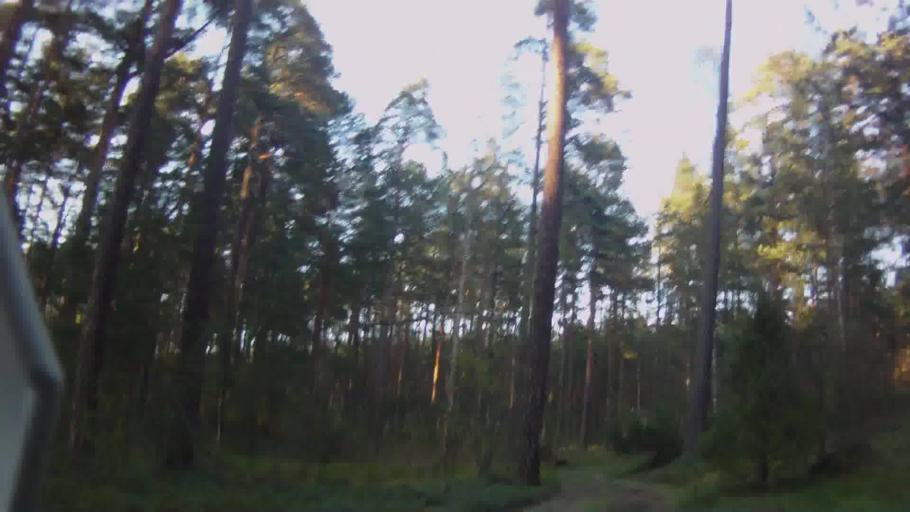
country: LV
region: Riga
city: Jaunciems
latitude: 57.0590
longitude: 24.1742
